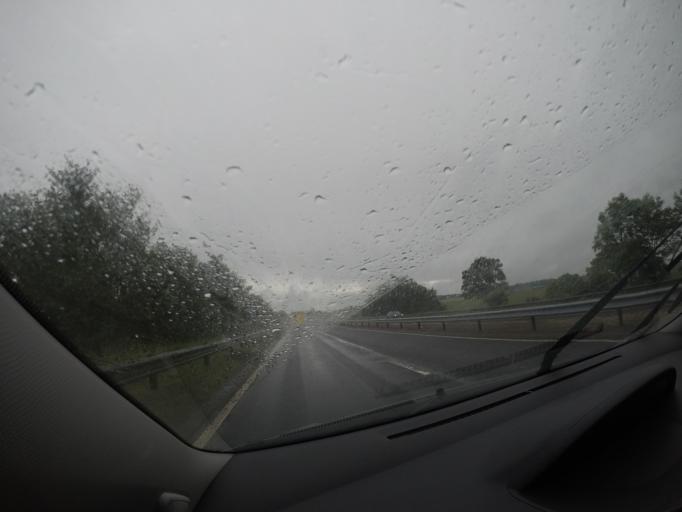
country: GB
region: Scotland
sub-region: Dundee City
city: Dundee
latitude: 56.5146
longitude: -2.9450
